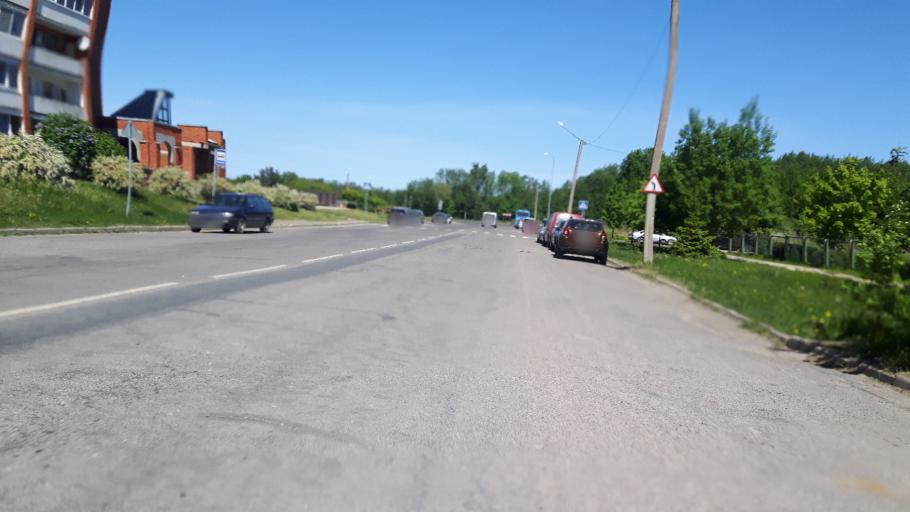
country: EE
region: Ida-Virumaa
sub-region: Sillamaee linn
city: Sillamae
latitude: 59.3928
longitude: 27.7972
